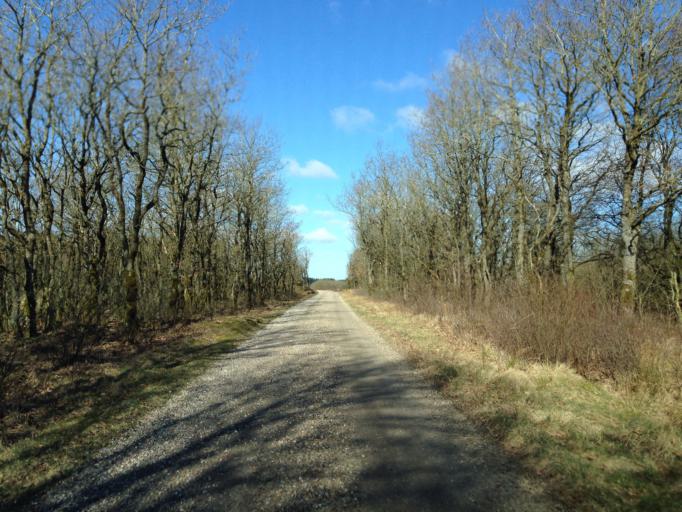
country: DK
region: Central Jutland
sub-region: Holstebro Kommune
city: Holstebro
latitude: 56.2534
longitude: 8.5081
